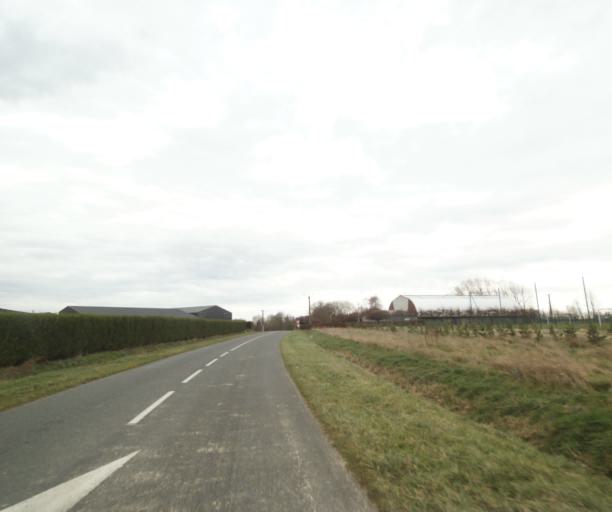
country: FR
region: Nord-Pas-de-Calais
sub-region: Departement du Nord
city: Sebourg
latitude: 50.3384
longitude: 3.6347
